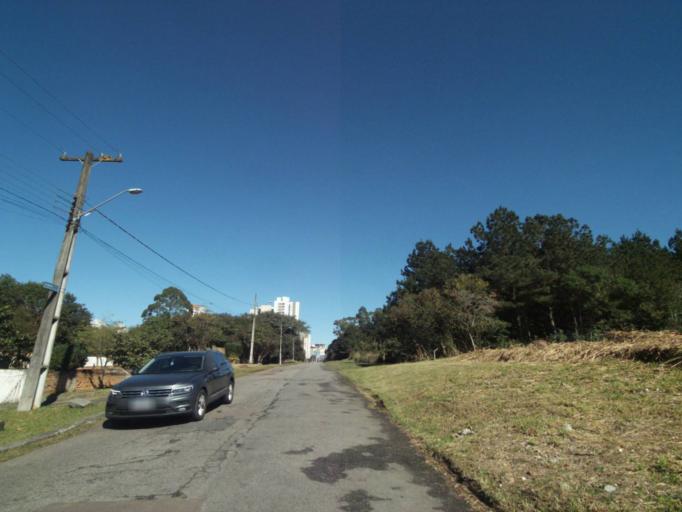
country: BR
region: Parana
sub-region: Curitiba
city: Curitiba
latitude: -25.4028
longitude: -49.2520
